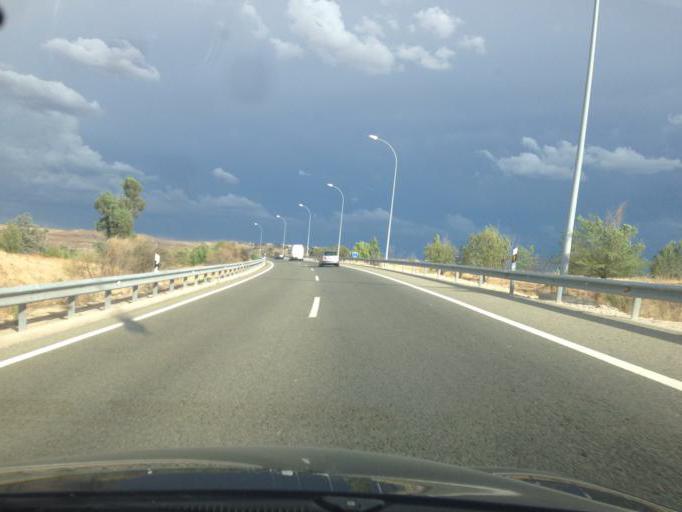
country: ES
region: Madrid
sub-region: Provincia de Madrid
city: San Sebastian de los Reyes
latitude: 40.5438
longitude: -3.5709
